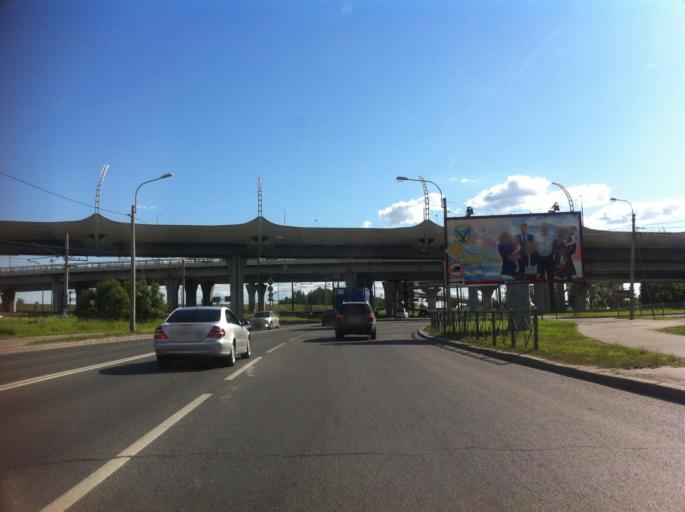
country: RU
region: St.-Petersburg
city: Dachnoye
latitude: 59.8365
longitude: 30.2690
